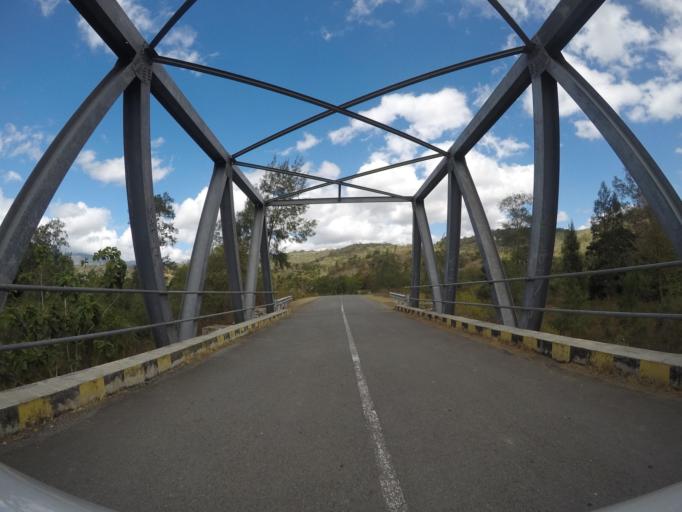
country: TL
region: Lautem
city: Lospalos
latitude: -8.4676
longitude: 126.8197
